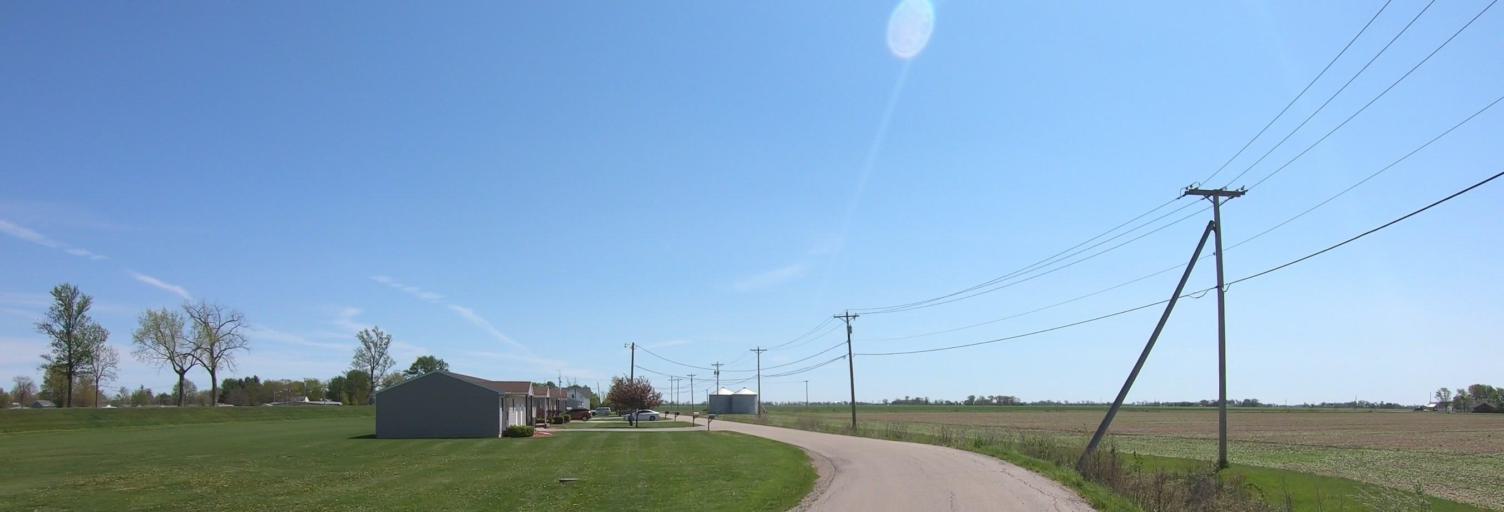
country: US
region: Ohio
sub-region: Henry County
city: Deshler
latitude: 41.2001
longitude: -83.9053
